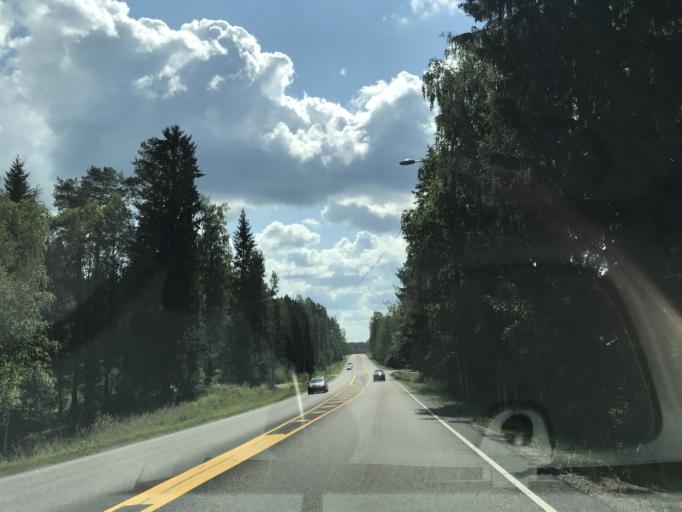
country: FI
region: Paijanne Tavastia
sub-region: Lahti
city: Lahti
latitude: 61.0376
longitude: 25.6684
